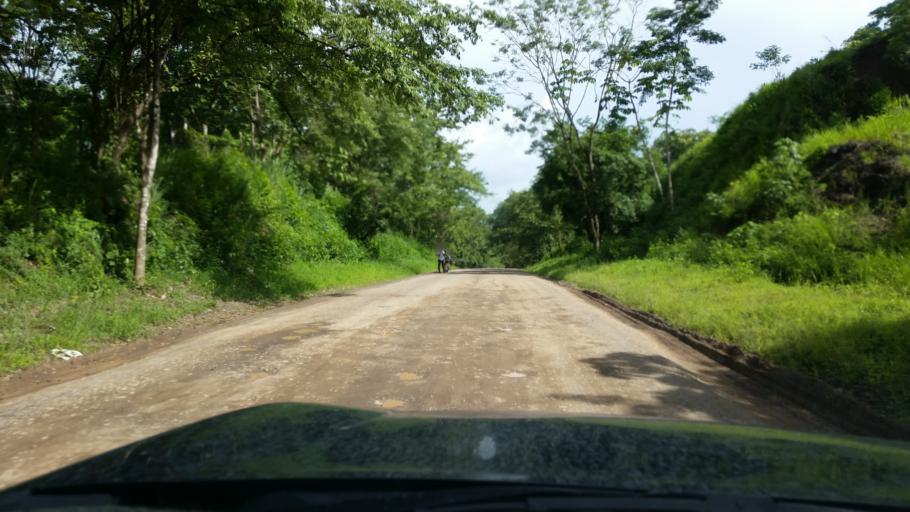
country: NI
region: Atlantico Norte (RAAN)
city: Siuna
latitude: 13.6673
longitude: -84.7924
